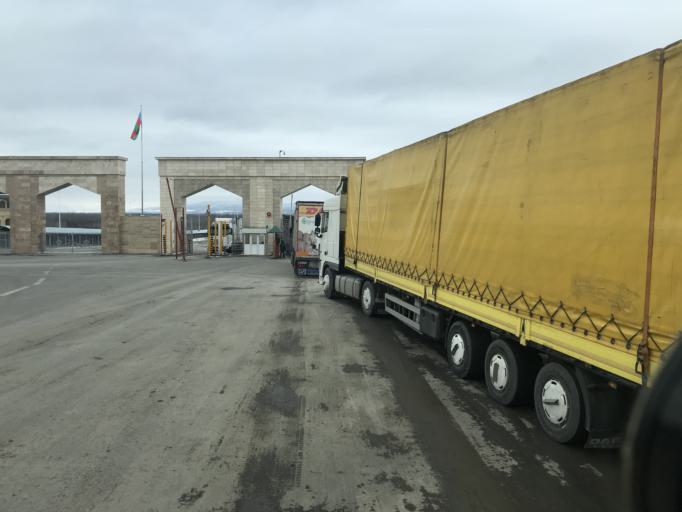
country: AZ
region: Qusar
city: Samur
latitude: 41.6377
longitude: 48.4197
